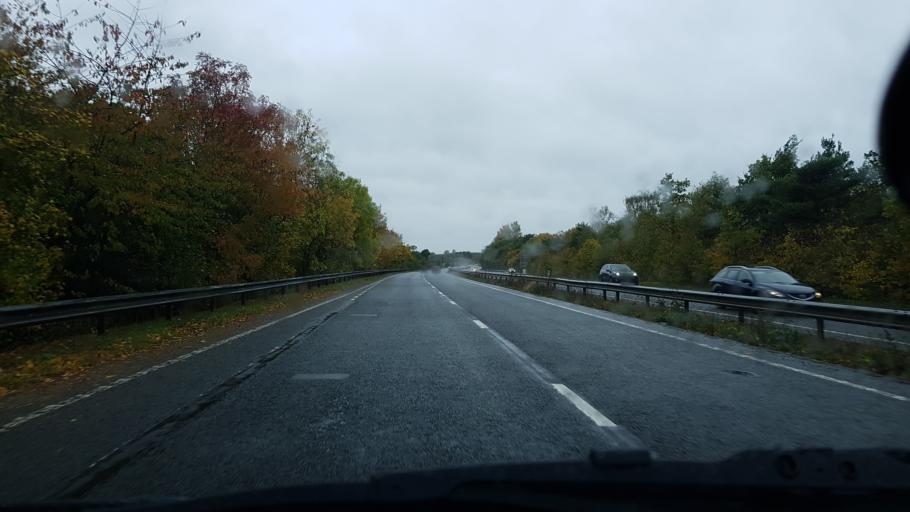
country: GB
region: England
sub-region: Oxfordshire
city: Witney
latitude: 51.7753
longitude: -1.4932
